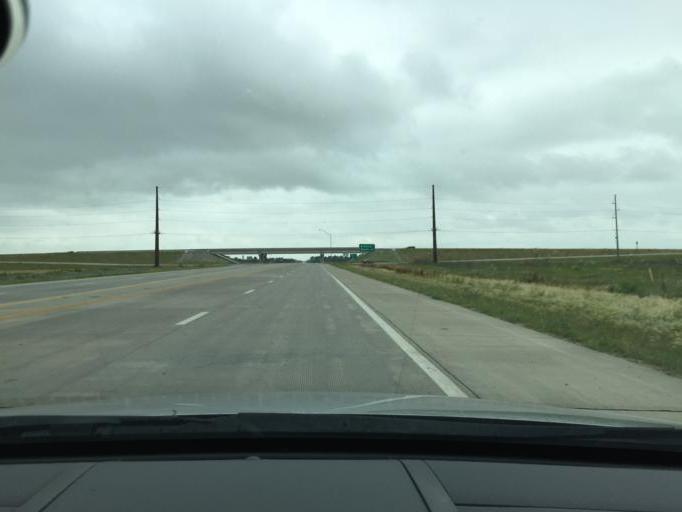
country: US
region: Kansas
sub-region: Reno County
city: Hutchinson
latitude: 38.0316
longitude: -97.8669
